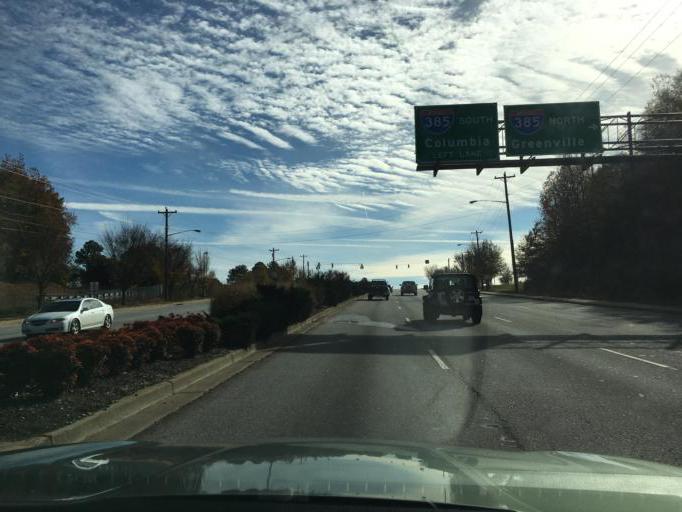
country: US
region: South Carolina
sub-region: Greenville County
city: Greenville
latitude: 34.8611
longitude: -82.3567
